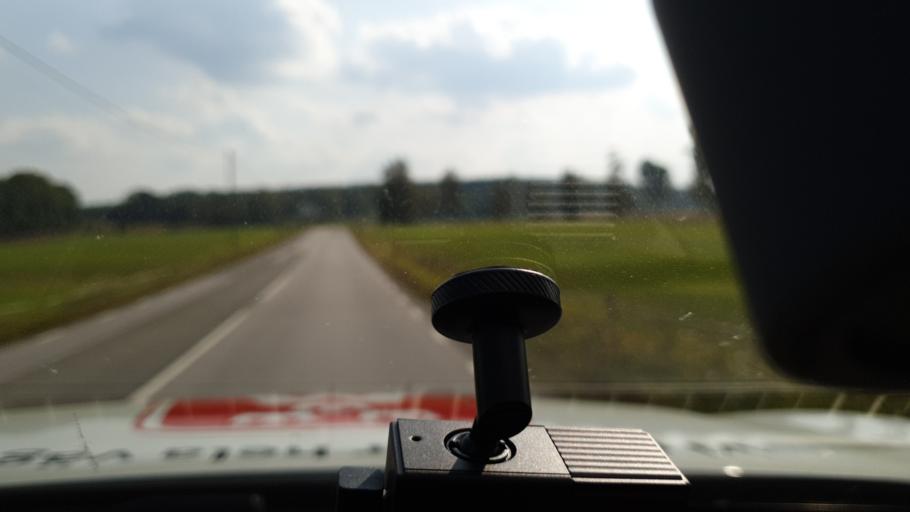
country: SE
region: Kalmar
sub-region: Vimmerby Kommun
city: Sodra Vi
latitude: 57.7472
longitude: 15.8312
